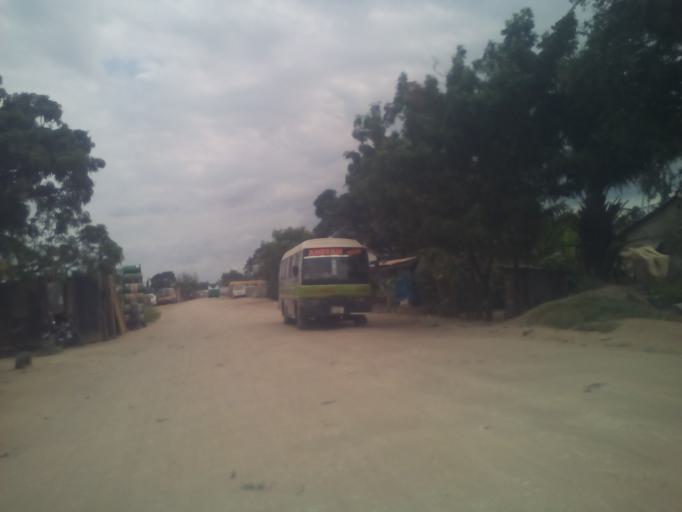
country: TZ
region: Dar es Salaam
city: Dar es Salaam
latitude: -6.8677
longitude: 39.2328
